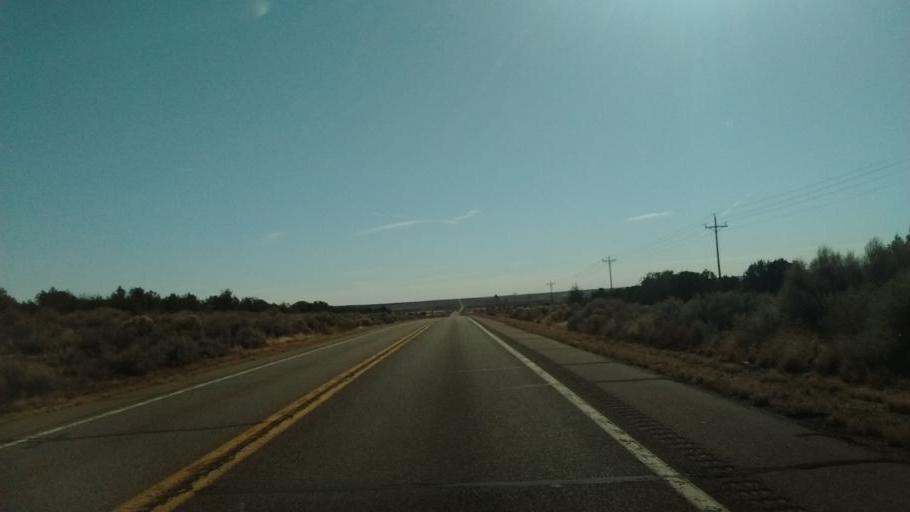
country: US
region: Arizona
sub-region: Mohave County
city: Colorado City
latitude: 36.9586
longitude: -112.9654
